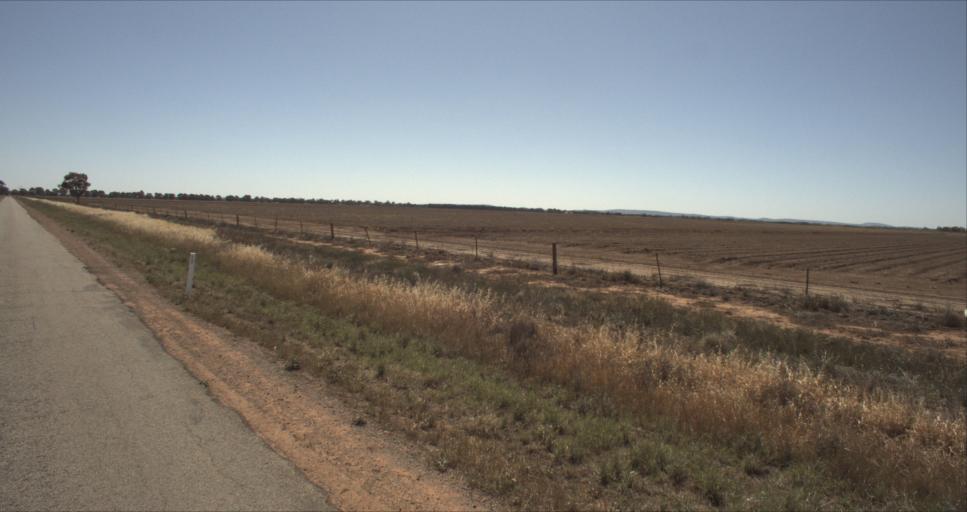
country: AU
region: New South Wales
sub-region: Leeton
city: Leeton
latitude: -34.5645
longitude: 146.3121
